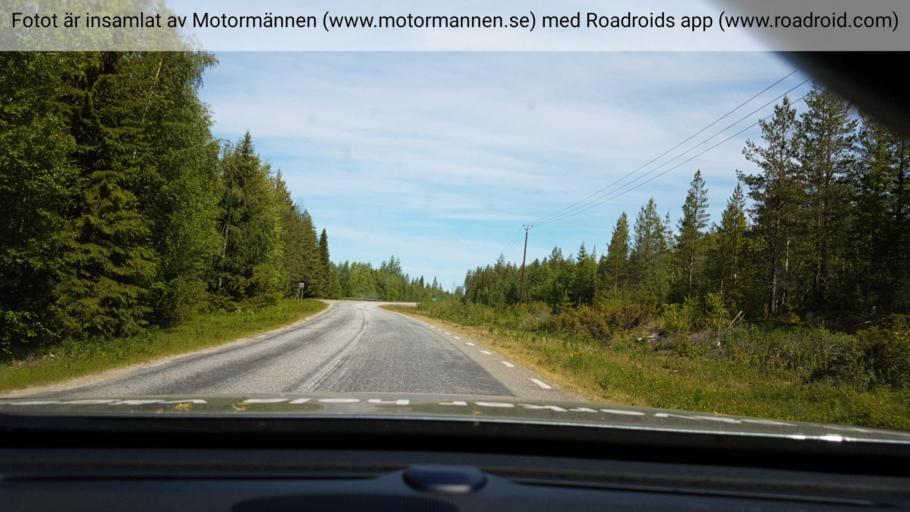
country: SE
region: Vaesterbotten
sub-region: Vilhelmina Kommun
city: Sjoberg
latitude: 64.4942
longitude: 15.9376
